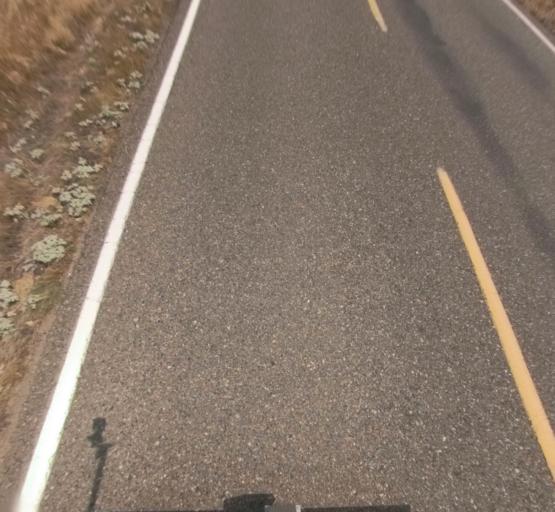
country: US
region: California
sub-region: Madera County
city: Madera Acres
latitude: 37.0770
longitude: -119.9668
